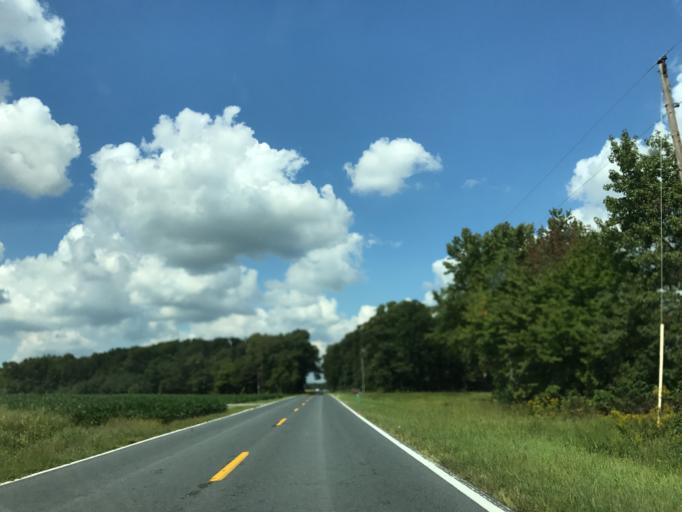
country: US
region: Maryland
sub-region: Caroline County
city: Ridgely
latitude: 39.0375
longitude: -75.9080
